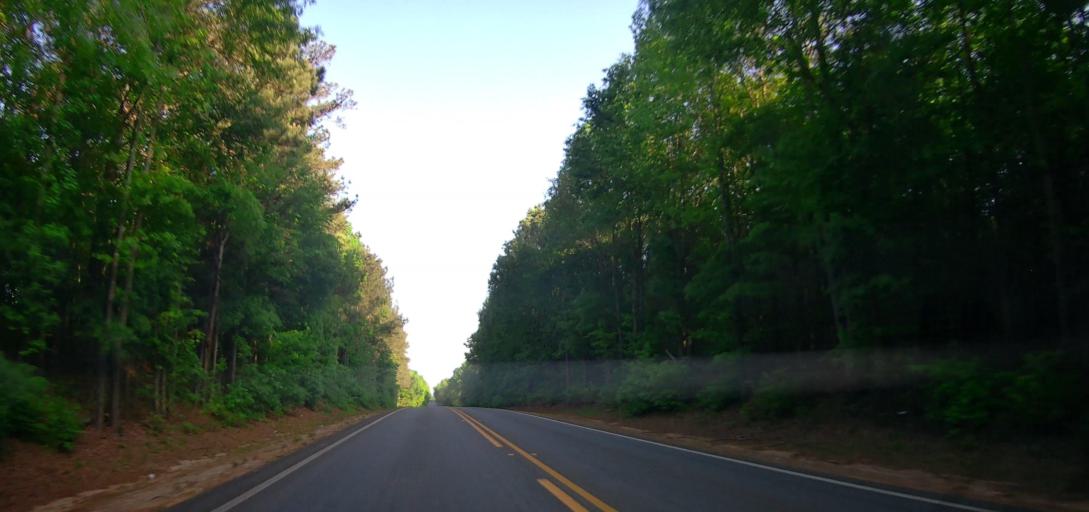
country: US
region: Georgia
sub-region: Putnam County
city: Eatonton
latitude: 33.3656
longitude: -83.5278
